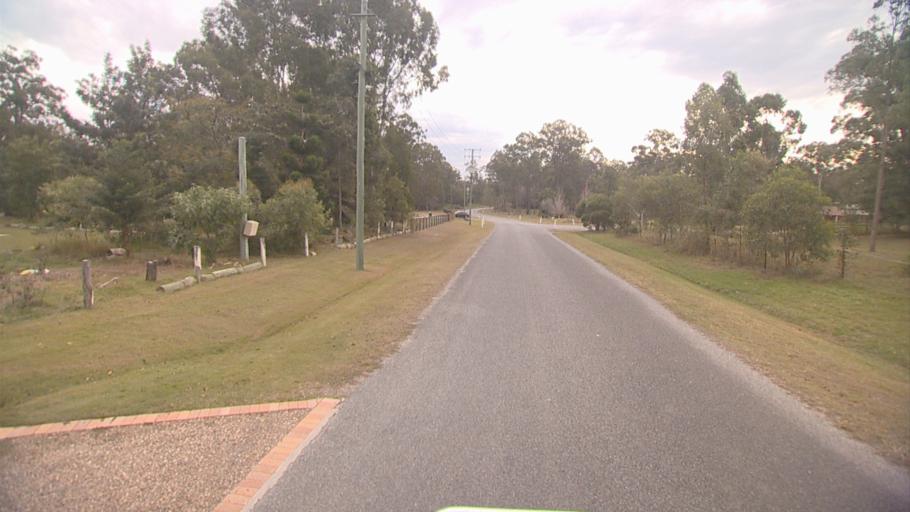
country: AU
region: Queensland
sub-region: Logan
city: Chambers Flat
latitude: -27.8020
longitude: 153.1288
